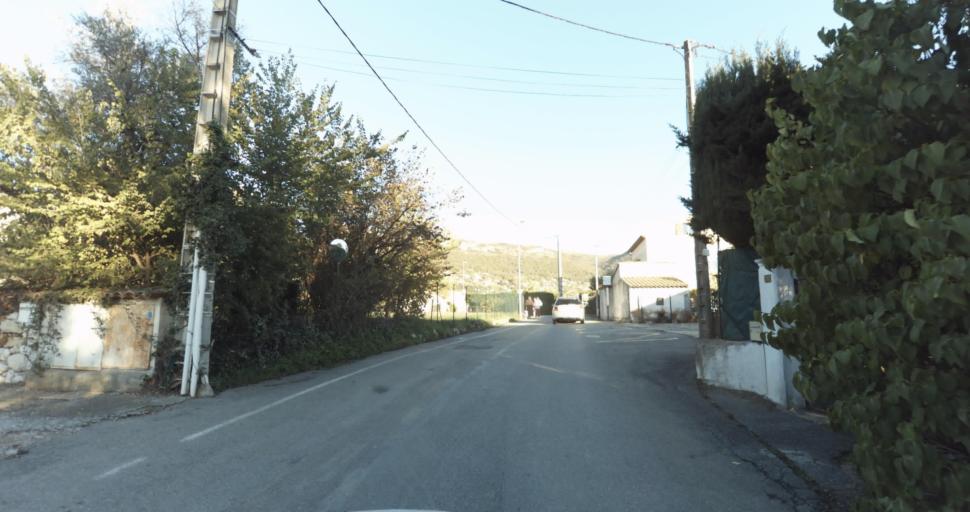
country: FR
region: Provence-Alpes-Cote d'Azur
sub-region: Departement des Alpes-Maritimes
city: Vence
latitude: 43.7207
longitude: 7.1237
